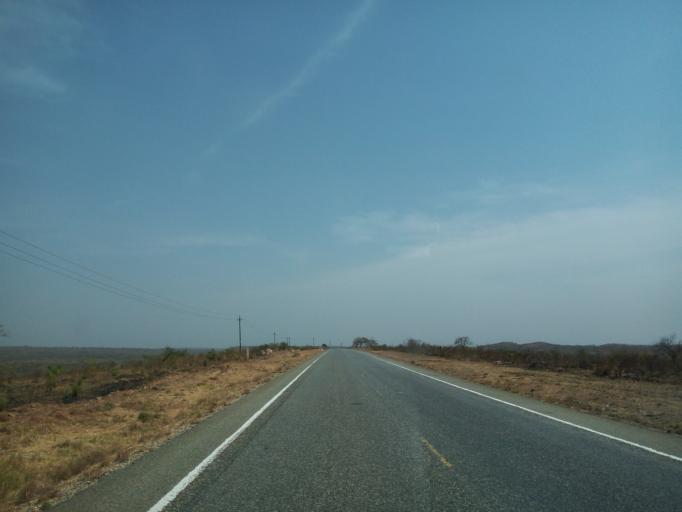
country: UG
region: Northern Region
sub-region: Nebbi District
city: Nebbi
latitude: 2.4407
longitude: 31.2520
